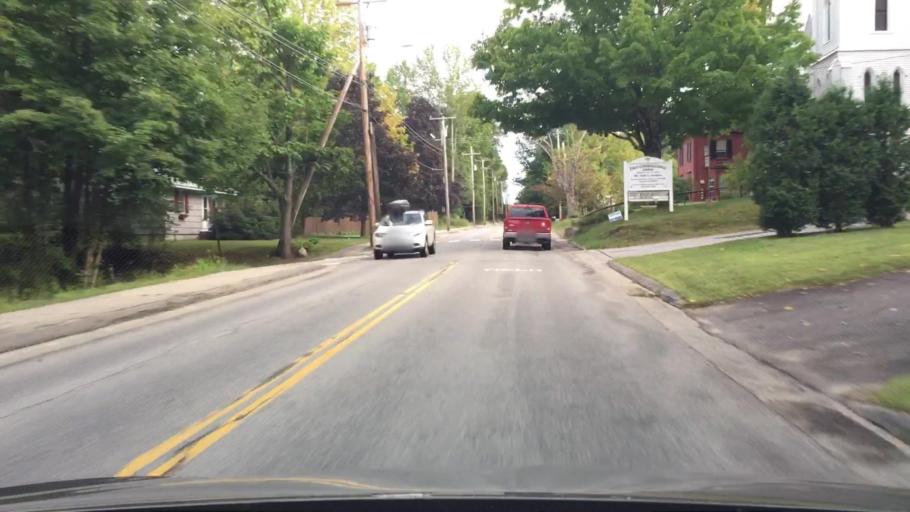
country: US
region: Maine
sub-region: Cumberland County
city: Bridgton
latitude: 44.0519
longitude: -70.7141
